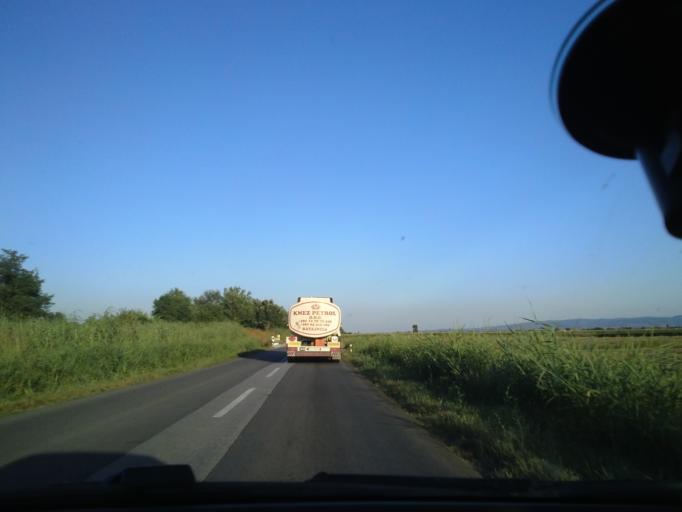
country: RS
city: Rumenka
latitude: 45.3124
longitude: 19.7211
